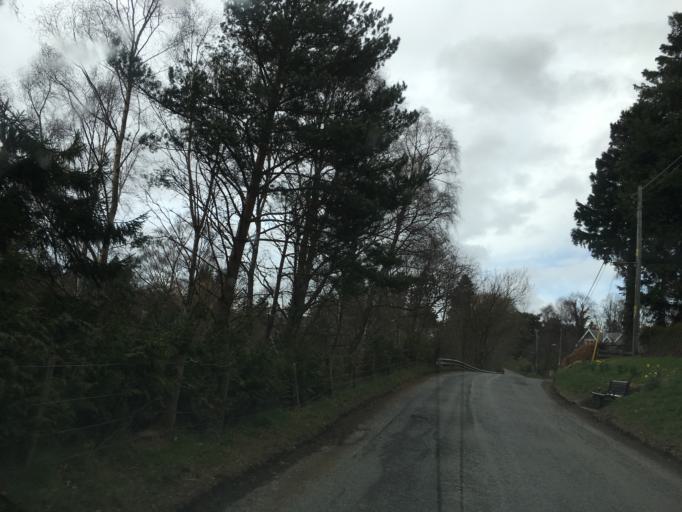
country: GB
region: Scotland
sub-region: Highland
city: Kingussie
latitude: 57.0816
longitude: -4.0524
